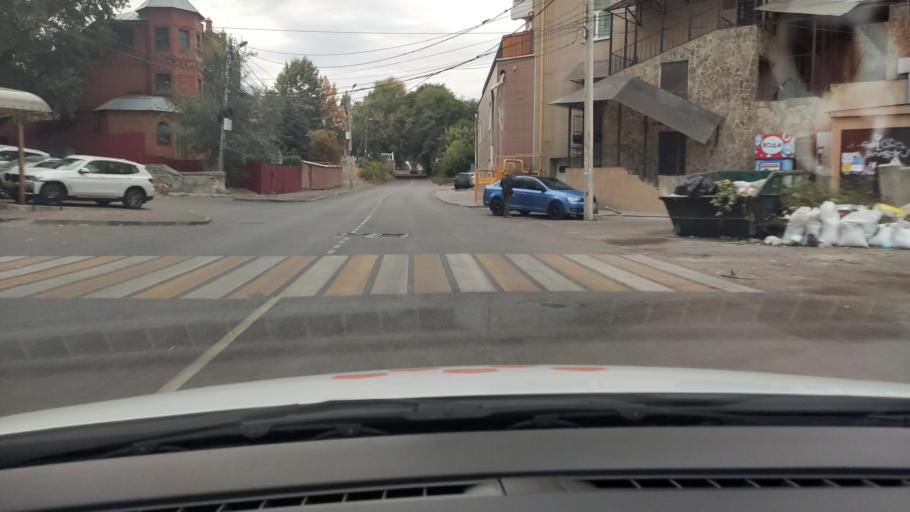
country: RU
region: Voronezj
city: Voronezh
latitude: 51.6696
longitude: 39.2133
